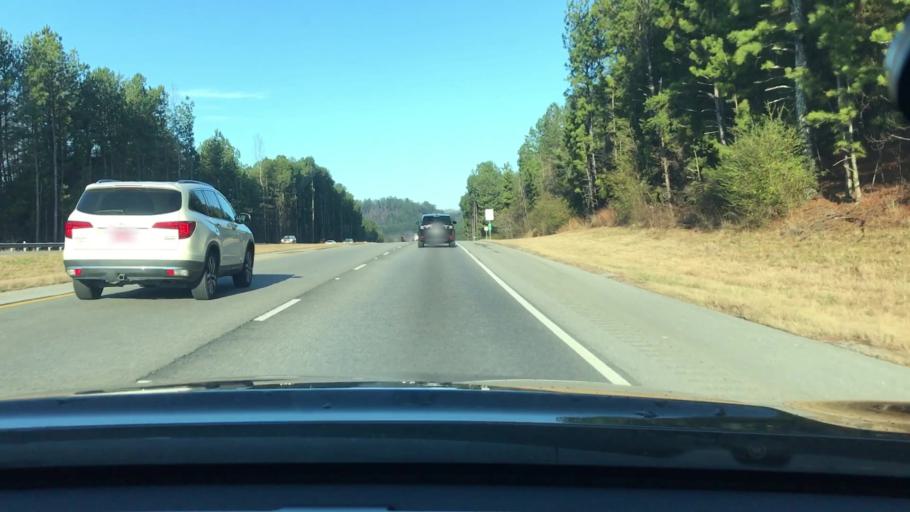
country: US
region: Alabama
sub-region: Shelby County
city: Chelsea
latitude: 33.3497
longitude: -86.6420
